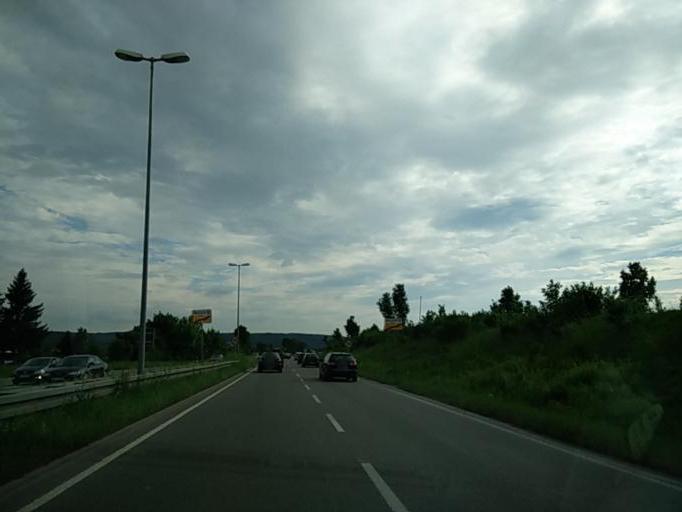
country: DE
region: Baden-Wuerttemberg
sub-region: Tuebingen Region
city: Tuebingen
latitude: 48.5083
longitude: 9.0413
